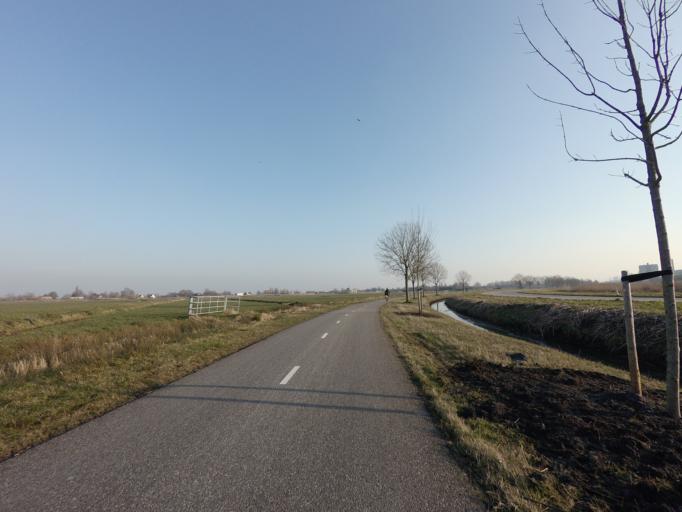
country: NL
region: North Holland
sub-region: Gemeente Haarlem
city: Haarlem
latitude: 52.3604
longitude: 4.6687
